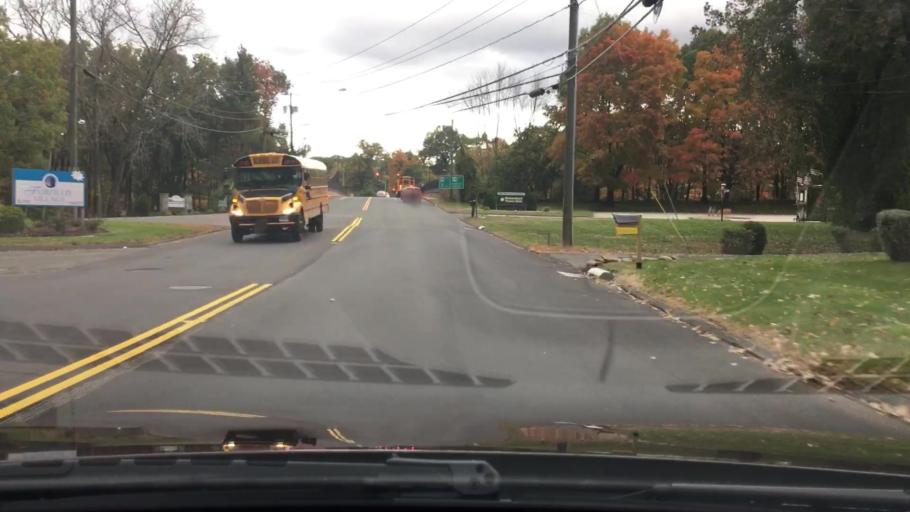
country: US
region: Connecticut
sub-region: Hartford County
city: Glastonbury Center
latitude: 41.7118
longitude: -72.5914
